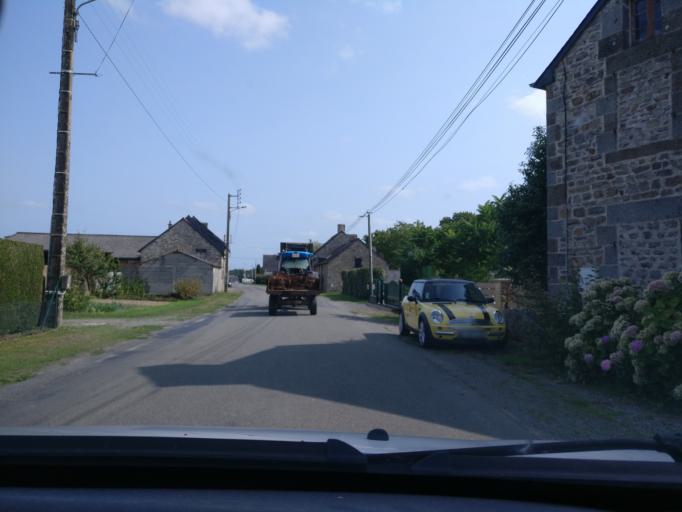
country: FR
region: Brittany
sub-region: Departement d'Ille-et-Vilaine
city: Gosne
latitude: 48.2484
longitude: -1.4713
